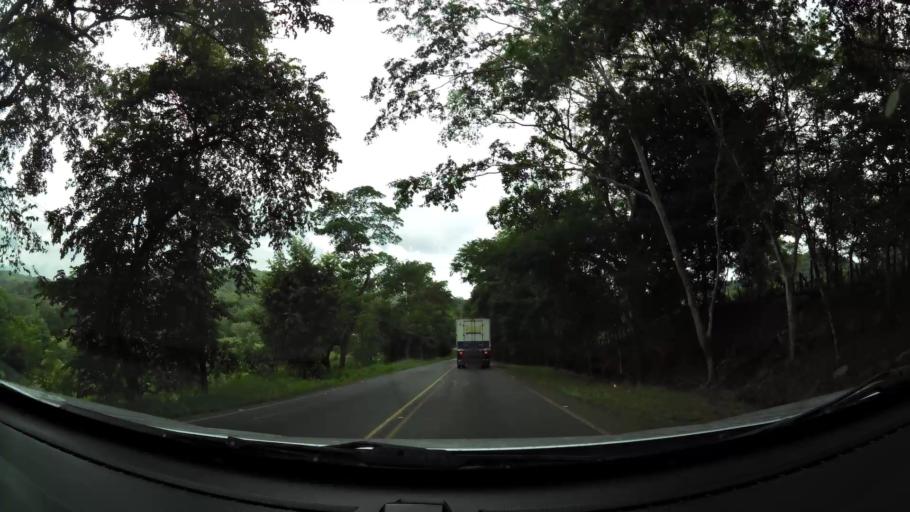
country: CR
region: Guanacaste
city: Juntas
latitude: 10.1656
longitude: -84.9197
